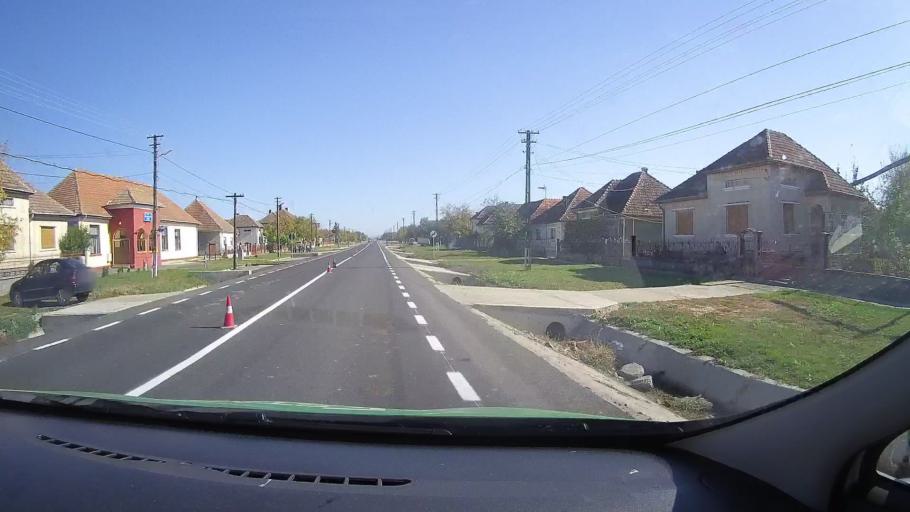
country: RO
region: Satu Mare
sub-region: Oras Ardud
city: Madaras
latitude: 47.6838
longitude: 22.8625
